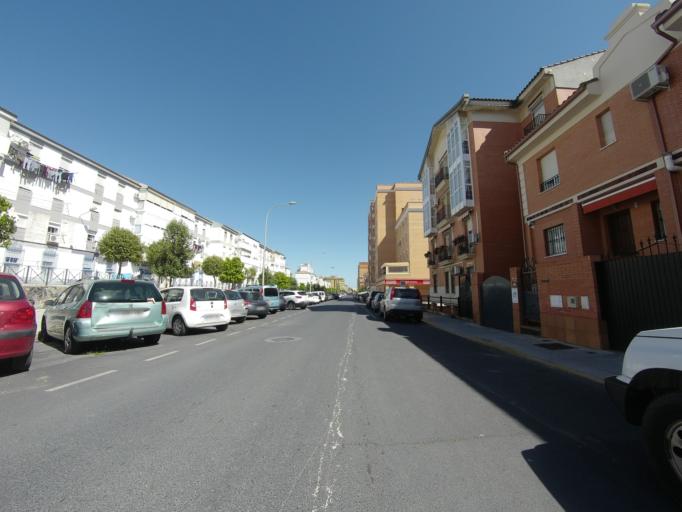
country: ES
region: Andalusia
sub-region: Provincia de Huelva
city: Huelva
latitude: 37.2680
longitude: -6.9370
